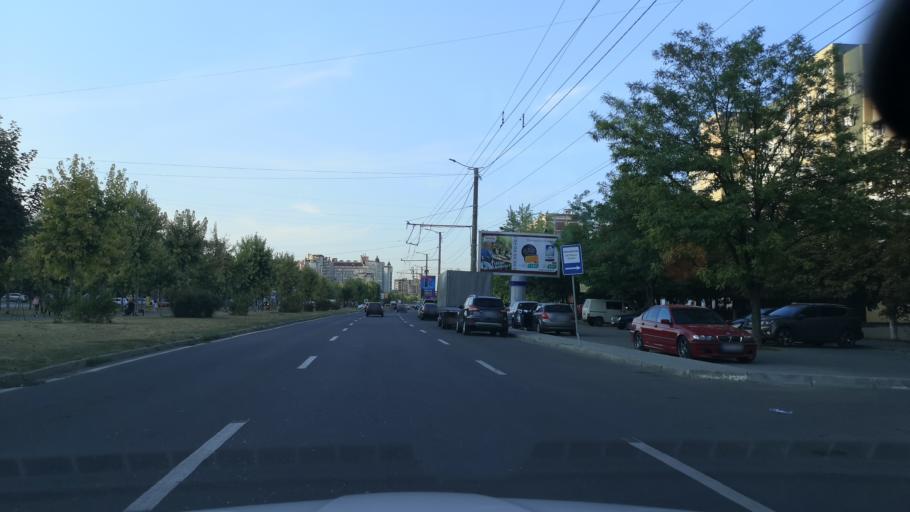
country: MD
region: Chisinau
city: Stauceni
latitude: 47.0483
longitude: 28.8907
